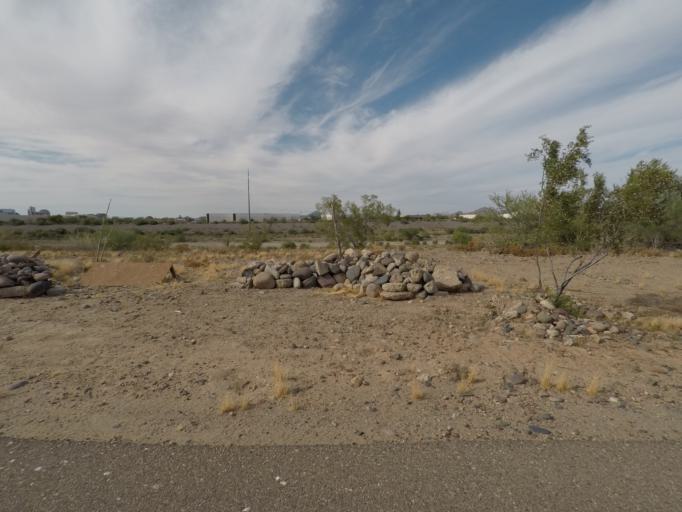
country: US
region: Arizona
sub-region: Maricopa County
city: Phoenix
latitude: 33.4179
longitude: -112.0541
